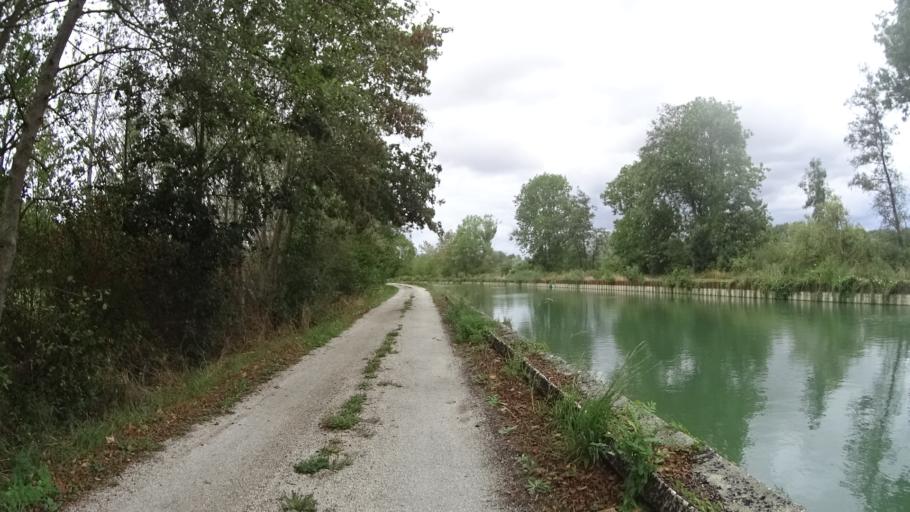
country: FR
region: Picardie
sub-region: Departement de l'Aisne
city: La Fere
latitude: 49.6946
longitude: 3.3702
